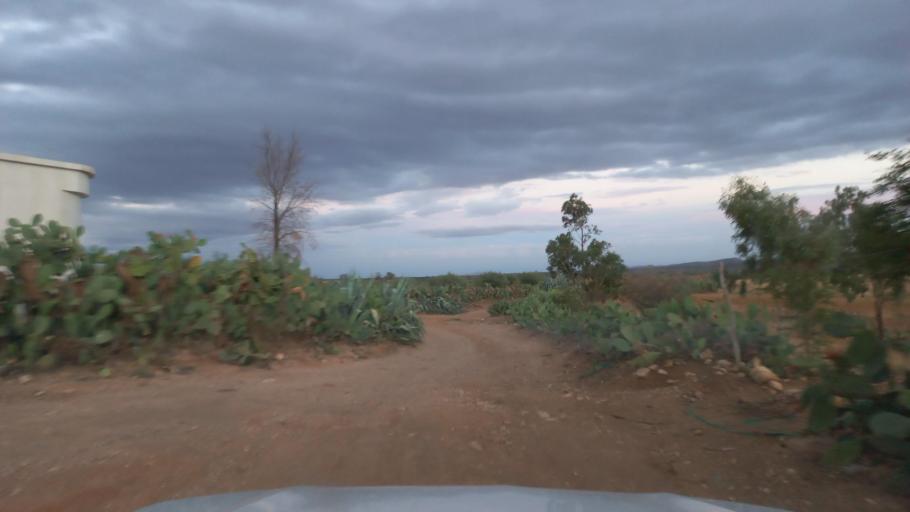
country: TN
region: Al Qasrayn
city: Kasserine
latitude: 35.2565
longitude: 8.9397
